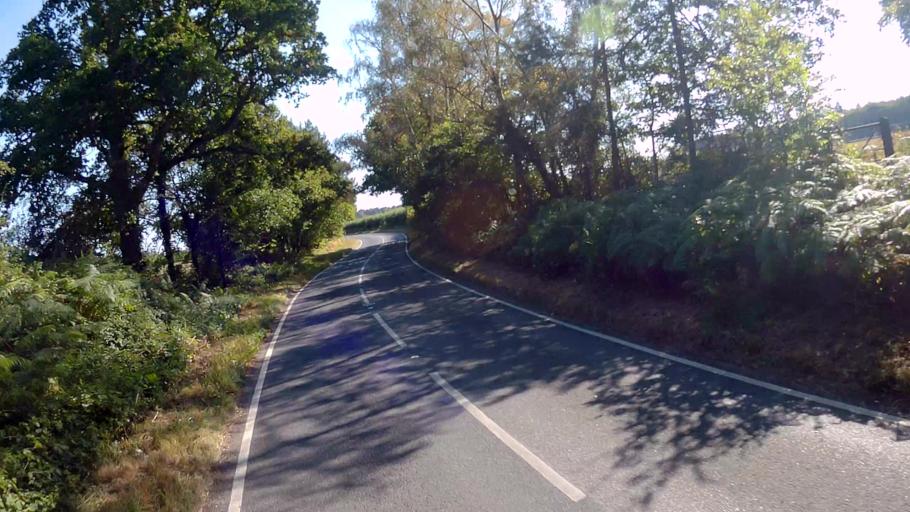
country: GB
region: England
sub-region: Surrey
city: Farnham
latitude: 51.1895
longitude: -0.7626
